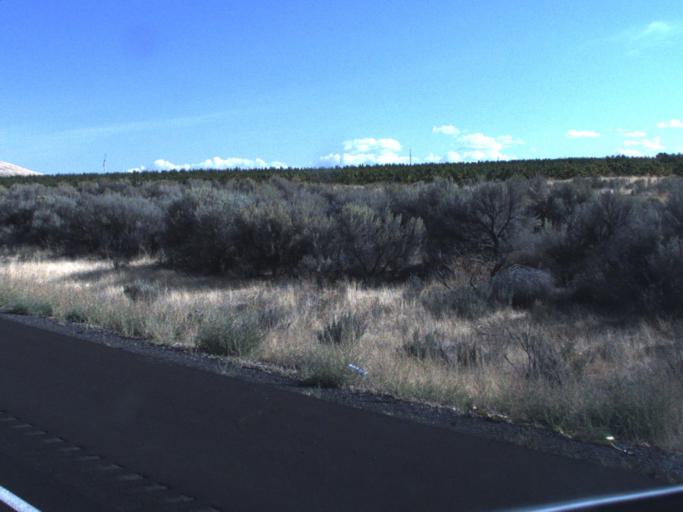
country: US
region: Washington
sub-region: Benton County
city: West Richland
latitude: 46.2617
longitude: -119.3986
